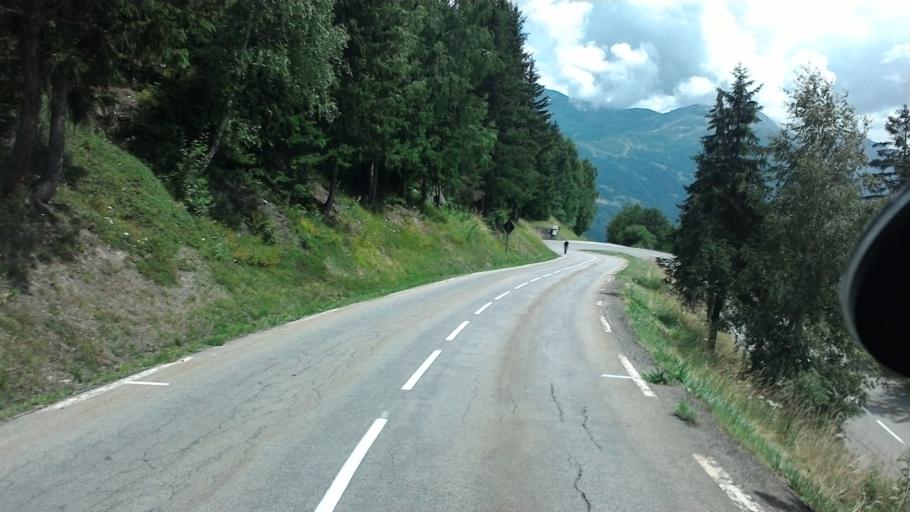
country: FR
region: Rhone-Alpes
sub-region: Departement de la Savoie
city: Seez
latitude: 45.6204
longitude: 6.8438
